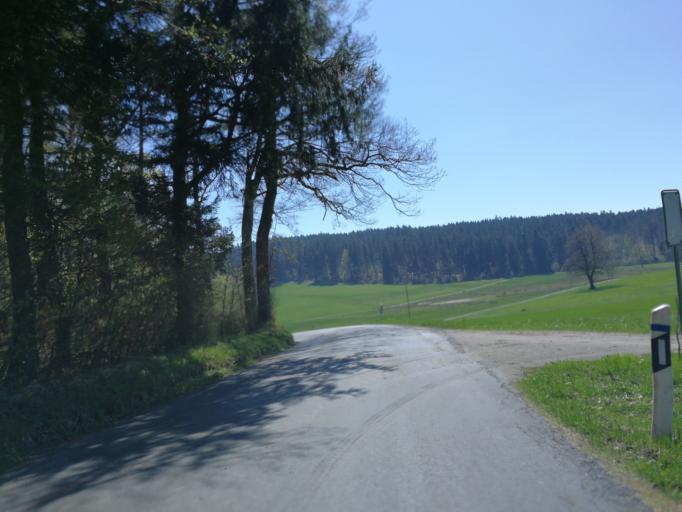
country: CH
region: Zurich
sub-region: Bezirk Uster
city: Aesch
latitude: 47.3119
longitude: 8.6595
